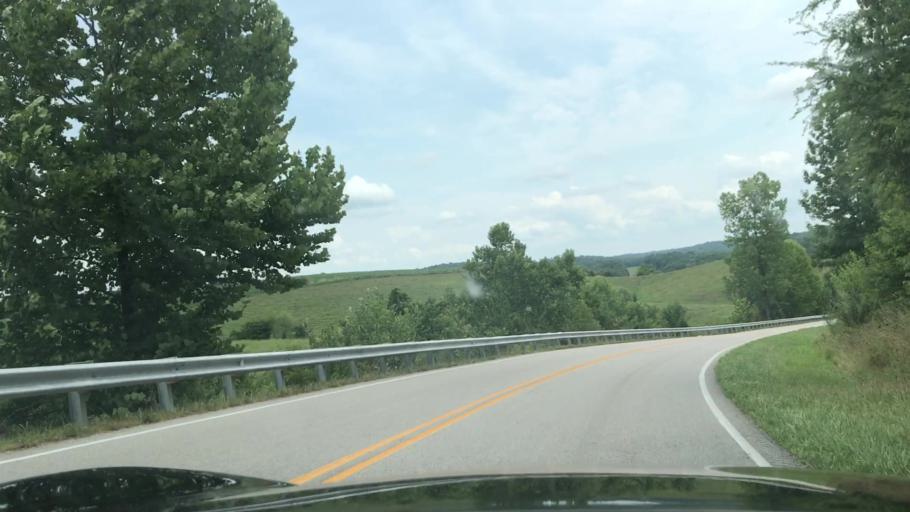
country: US
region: Kentucky
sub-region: Butler County
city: Morgantown
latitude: 37.1804
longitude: -86.8559
